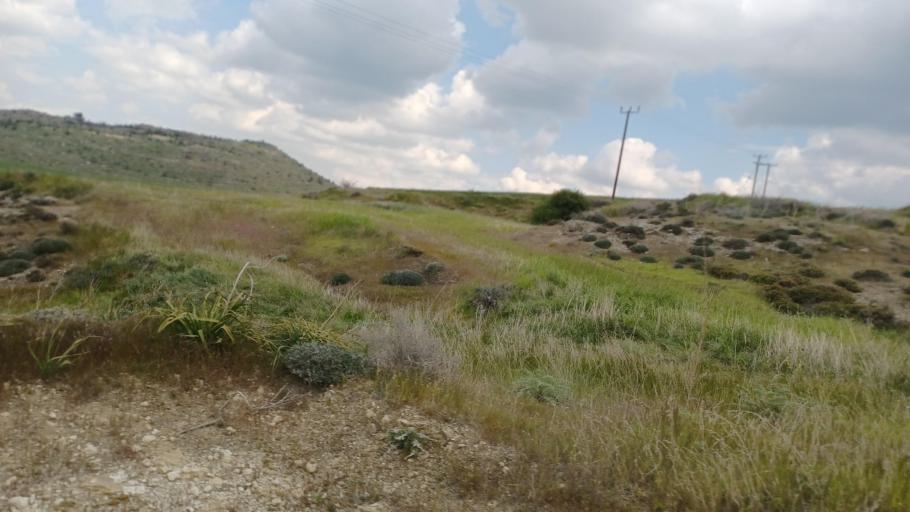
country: CY
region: Lefkosia
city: Lefka
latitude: 35.0837
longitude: 32.9503
